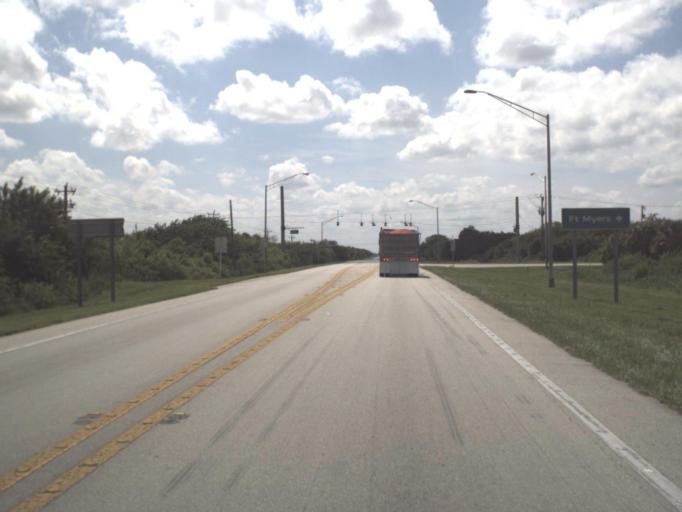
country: US
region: Florida
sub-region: Collier County
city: Immokalee
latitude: 26.4870
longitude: -81.4347
